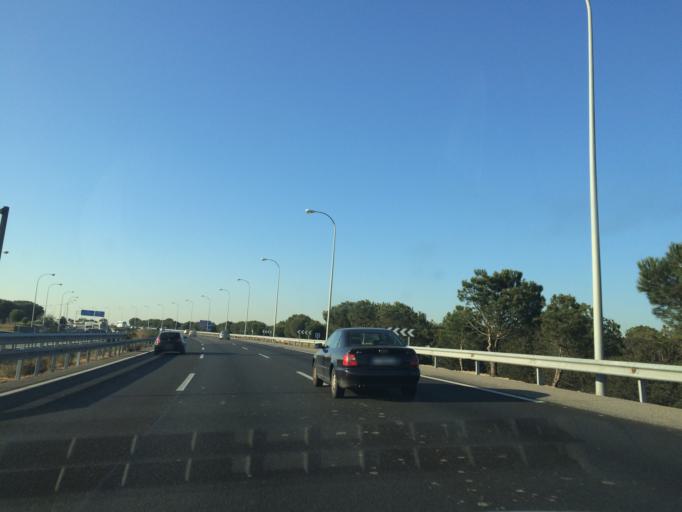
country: ES
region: Madrid
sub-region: Provincia de Madrid
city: Alcorcon
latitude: 40.3812
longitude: -3.8113
